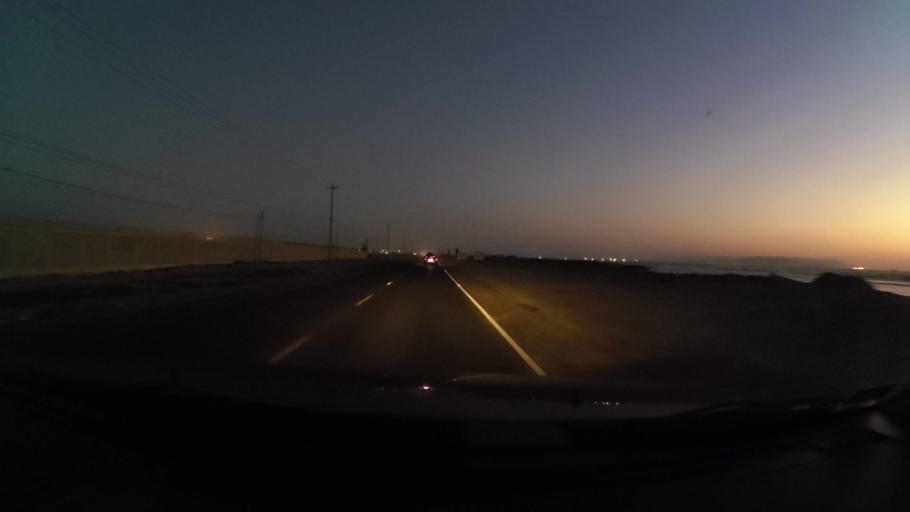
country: PE
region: Ica
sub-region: Provincia de Pisco
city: Pisco
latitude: -13.7574
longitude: -76.2316
